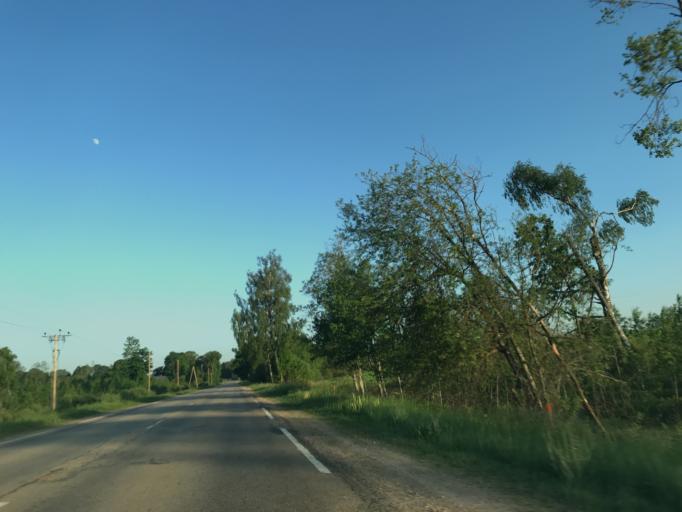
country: LV
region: Baldone
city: Baldone
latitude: 56.6972
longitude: 24.3841
